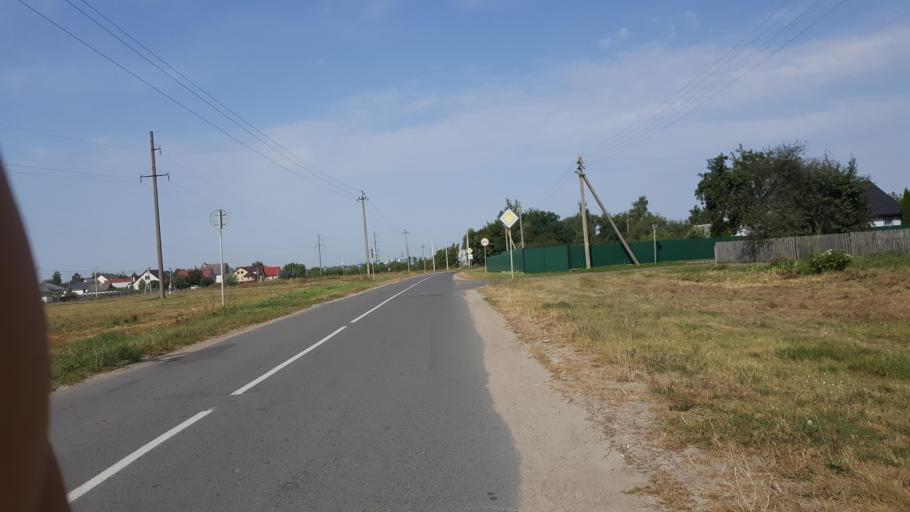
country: BY
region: Brest
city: Kamyanyets
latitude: 52.3943
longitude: 23.8144
